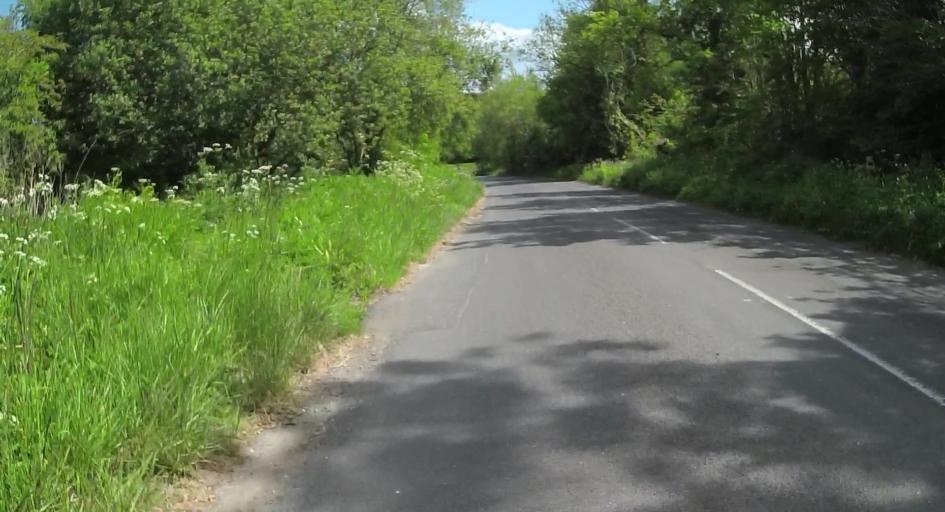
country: GB
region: England
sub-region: Hampshire
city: Fleet
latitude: 51.2451
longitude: -0.8678
